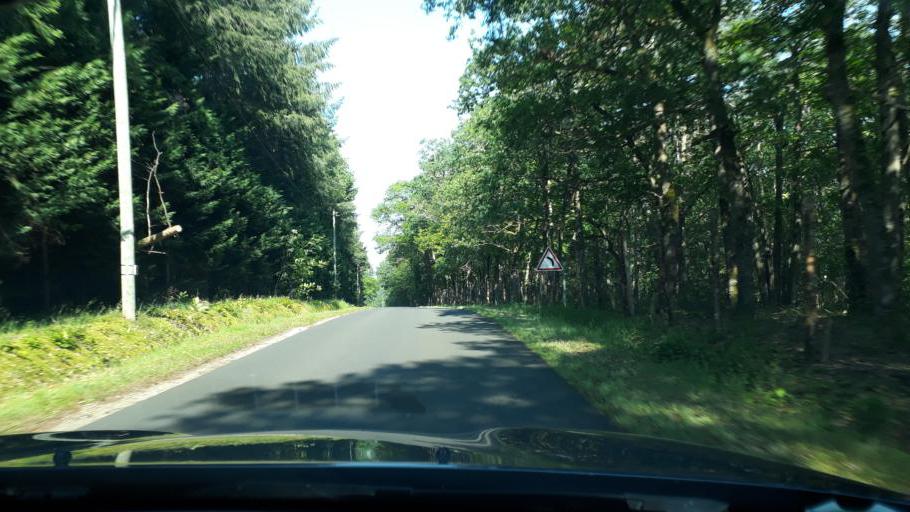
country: FR
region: Centre
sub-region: Departement du Loir-et-Cher
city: Dhuizon
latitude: 47.6248
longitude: 1.7163
